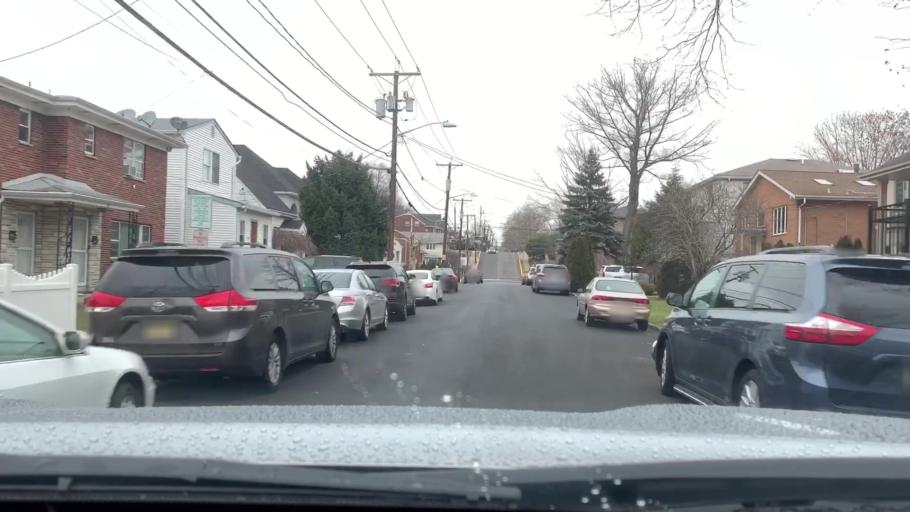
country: US
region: New Jersey
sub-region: Bergen County
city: Edgewater
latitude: 40.8393
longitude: -73.9847
